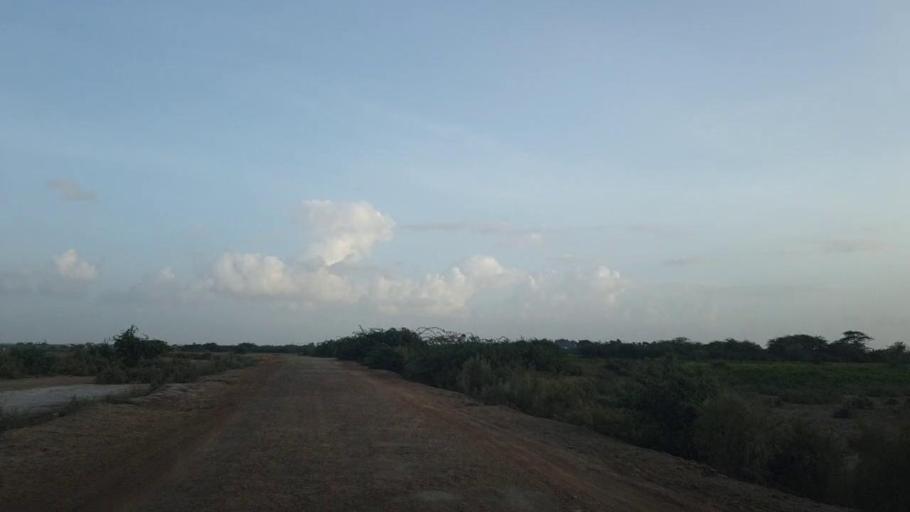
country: PK
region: Sindh
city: Kadhan
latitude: 24.5589
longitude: 69.1215
